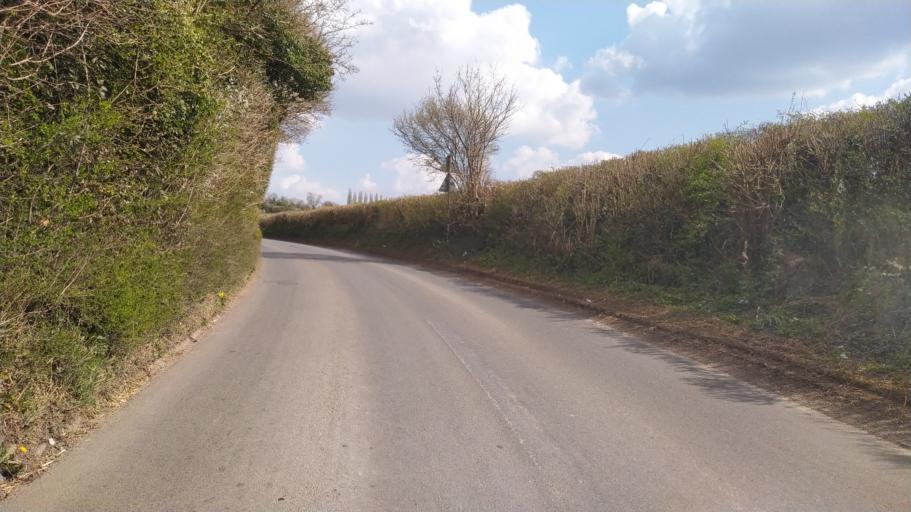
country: GB
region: England
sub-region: Somerset
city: Frome
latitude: 51.2318
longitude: -2.3484
